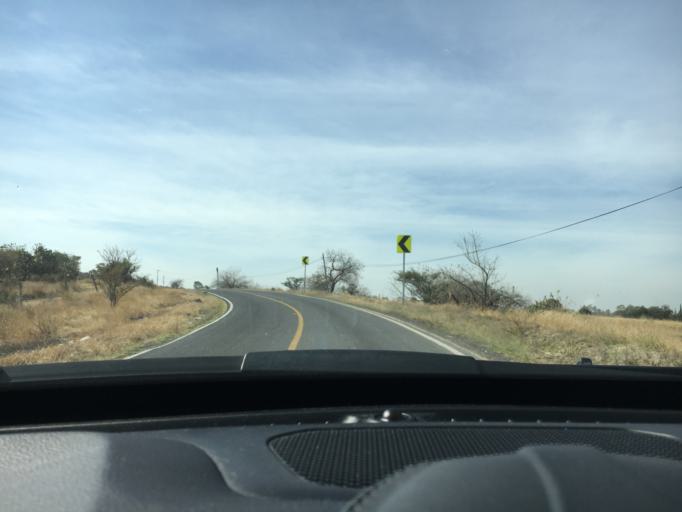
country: MX
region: Guanajuato
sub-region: Silao de la Victoria
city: San Francisco (Banos de Agua Caliente)
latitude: 21.0743
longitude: -101.4904
